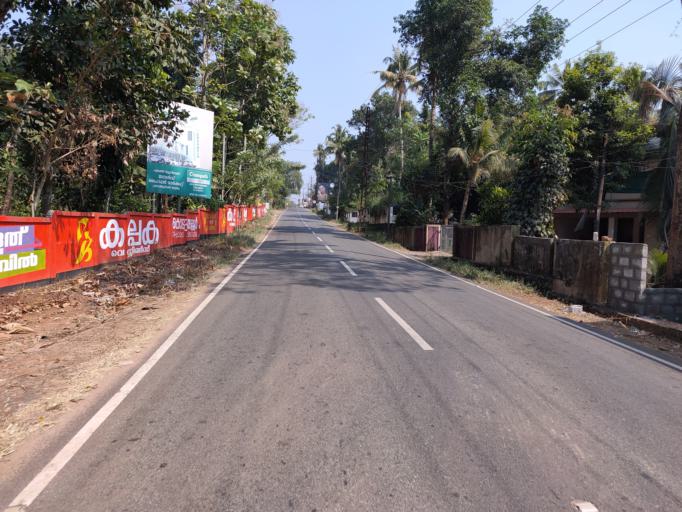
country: IN
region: Kerala
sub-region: Thrissur District
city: Kodungallur
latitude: 10.2327
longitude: 76.2812
